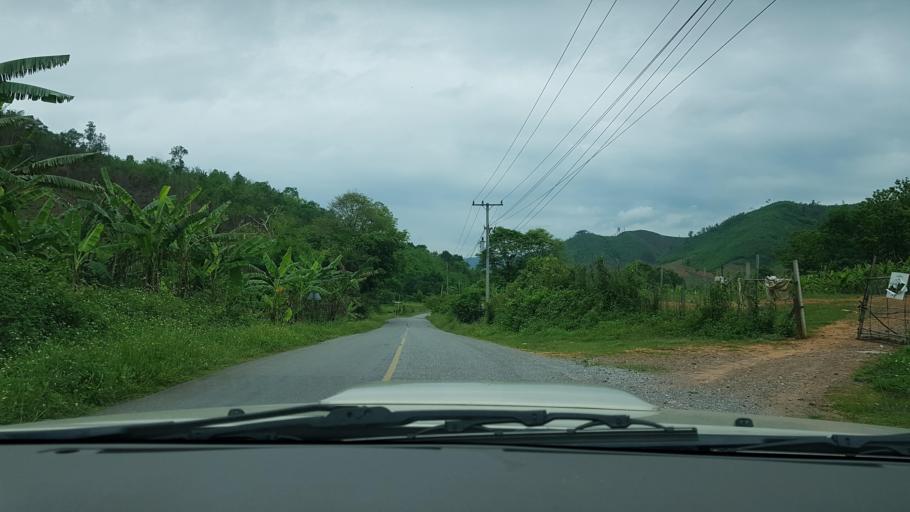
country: LA
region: Loungnamtha
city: Muang Nale
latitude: 20.3752
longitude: 101.7324
